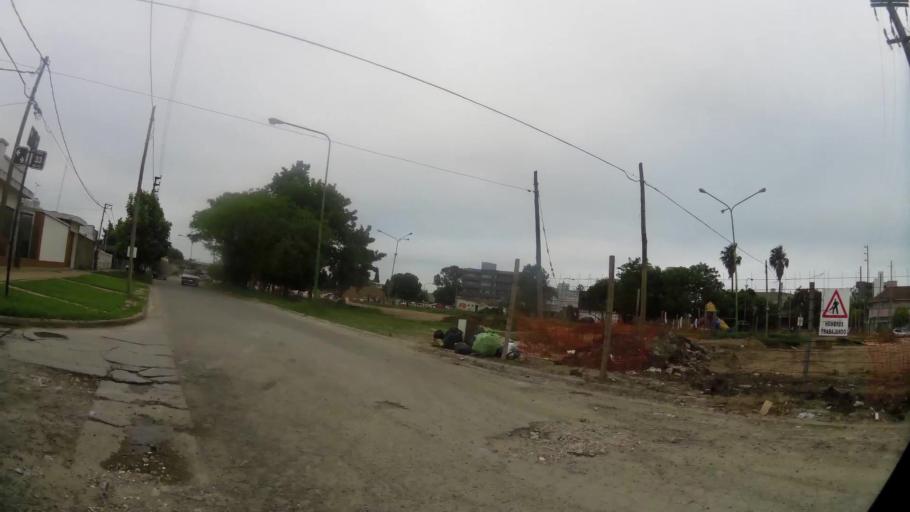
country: AR
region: Buenos Aires
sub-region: Partido de La Plata
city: La Plata
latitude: -34.9244
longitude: -57.9929
